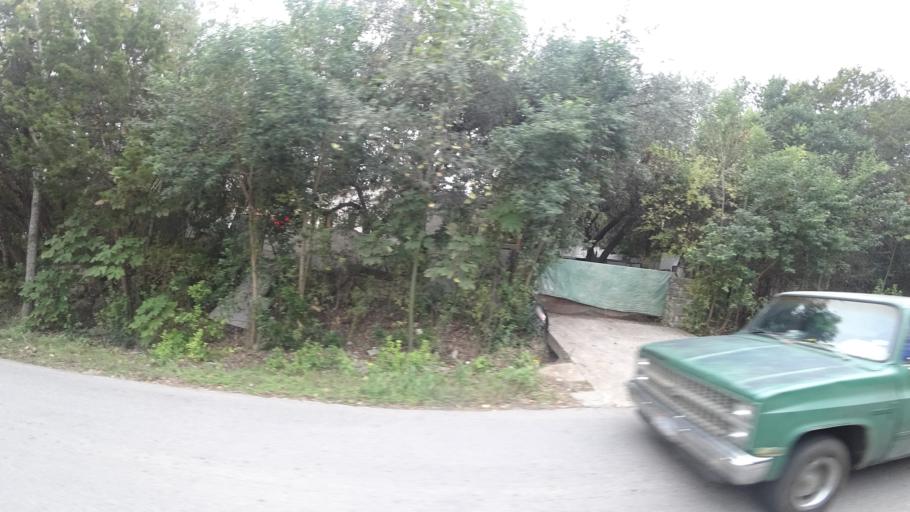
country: US
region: Texas
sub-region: Travis County
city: Hudson Bend
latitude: 30.3844
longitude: -97.9227
